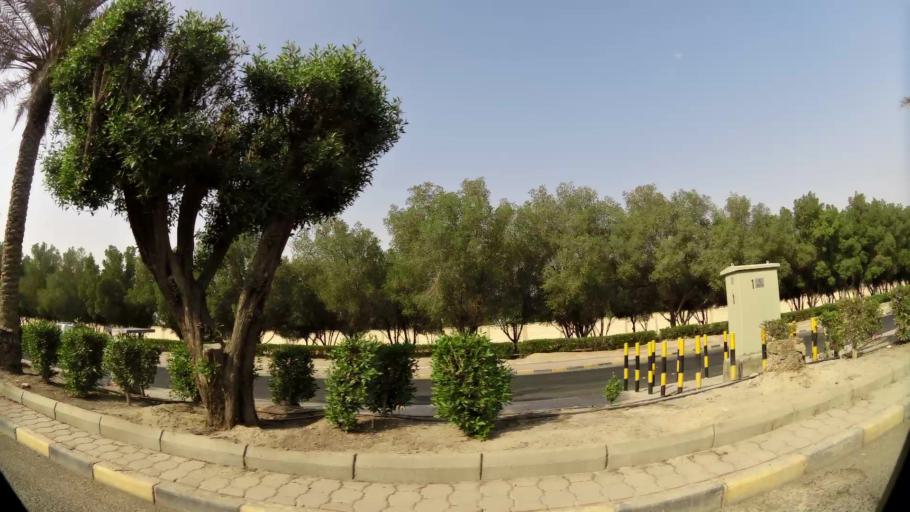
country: KW
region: Al Asimah
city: Ar Rabiyah
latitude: 29.3058
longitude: 47.8322
